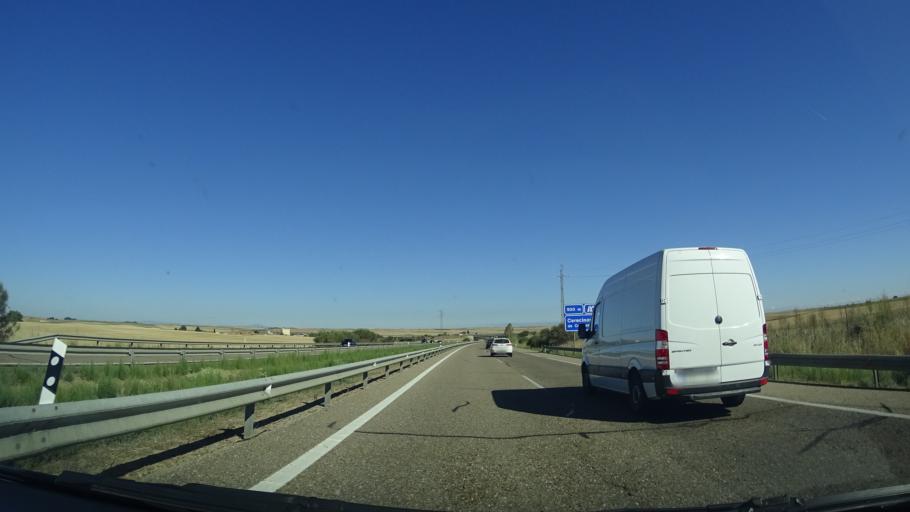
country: ES
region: Castille and Leon
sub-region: Provincia de Zamora
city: Cerecinos de Campos
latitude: 41.8933
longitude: -5.4704
